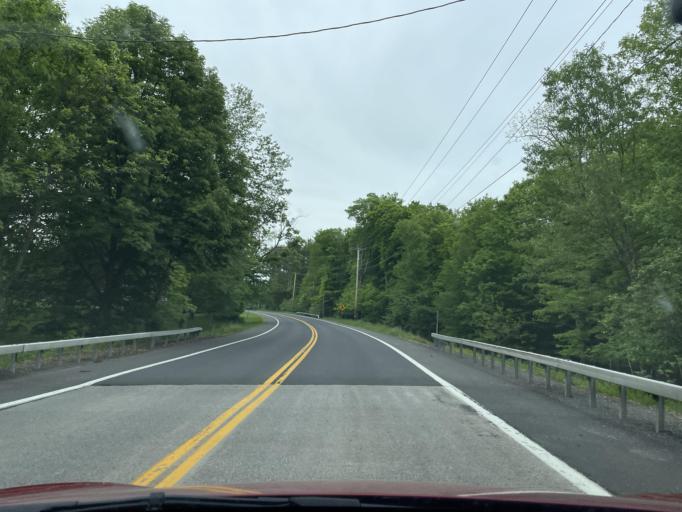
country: US
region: New York
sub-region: Ulster County
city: Manorville
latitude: 42.0762
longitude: -74.0230
